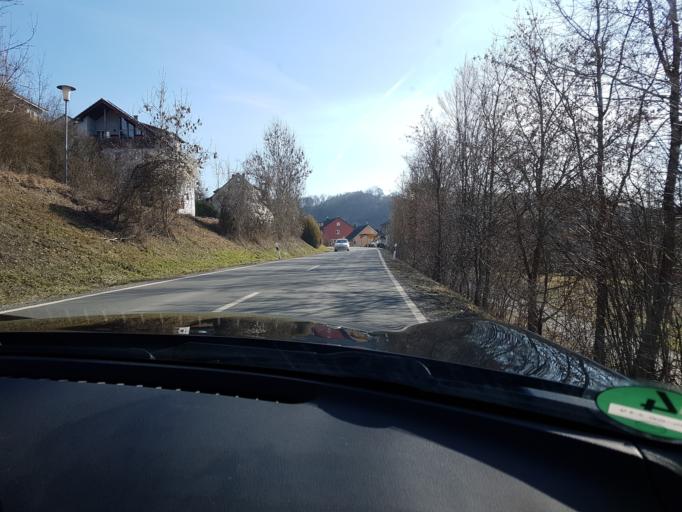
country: DE
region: Baden-Wuerttemberg
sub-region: Regierungsbezirk Stuttgart
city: Krautheim
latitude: 49.3707
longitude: 9.6573
